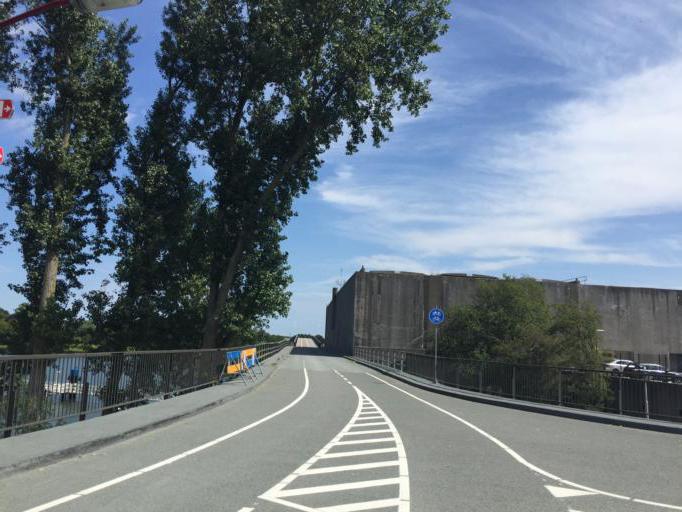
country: NL
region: Utrecht
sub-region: Gemeente Nieuwegein
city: Nieuwegein
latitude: 52.0344
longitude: 5.1136
